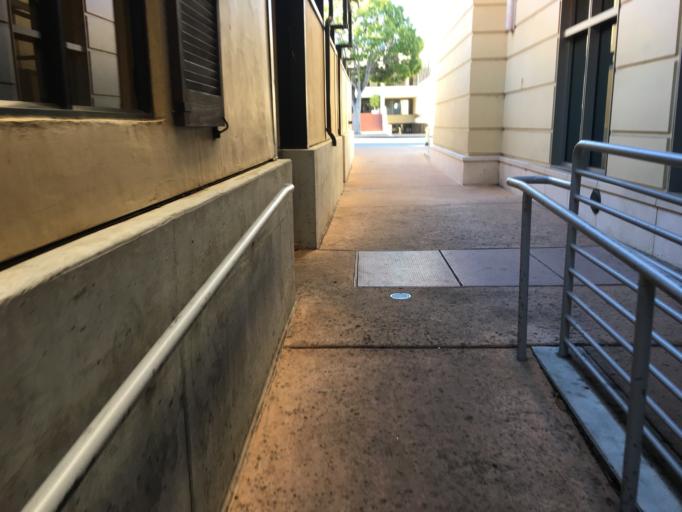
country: US
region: California
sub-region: San Luis Obispo County
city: San Luis Obispo
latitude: 35.2819
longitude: -120.6603
